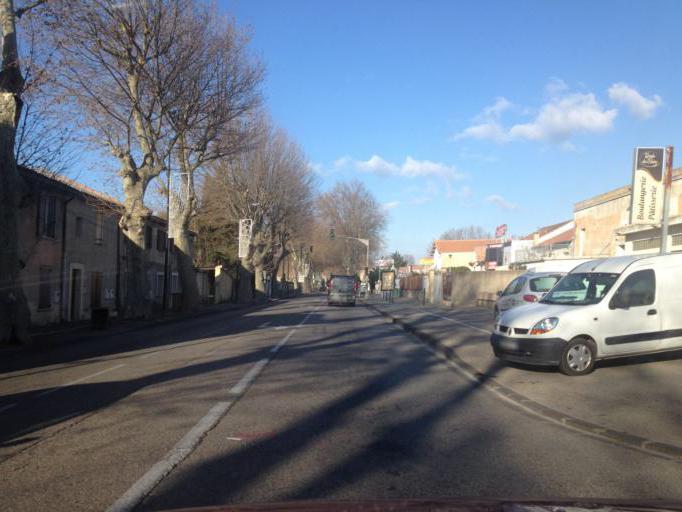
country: FR
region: Provence-Alpes-Cote d'Azur
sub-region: Departement du Vaucluse
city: Orange
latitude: 44.1312
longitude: 4.8164
